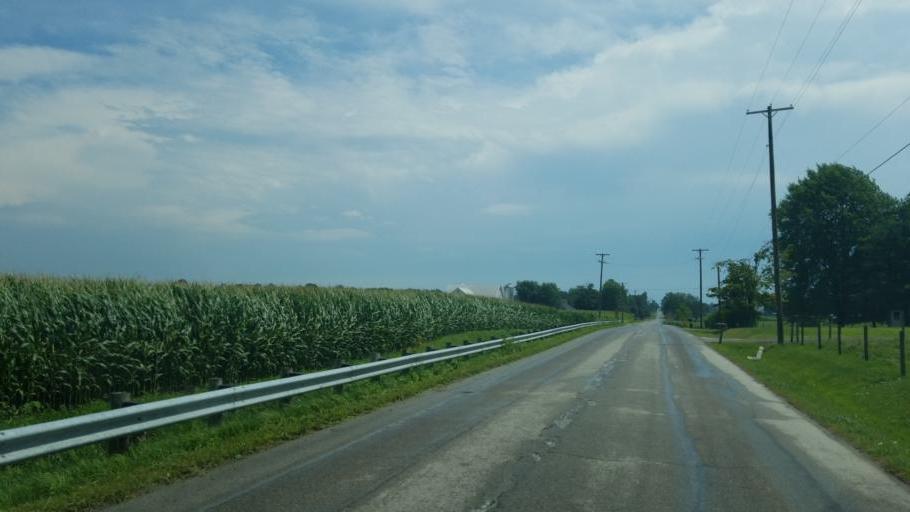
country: US
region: Ohio
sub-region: Geauga County
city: Middlefield
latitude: 41.4791
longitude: -81.0271
